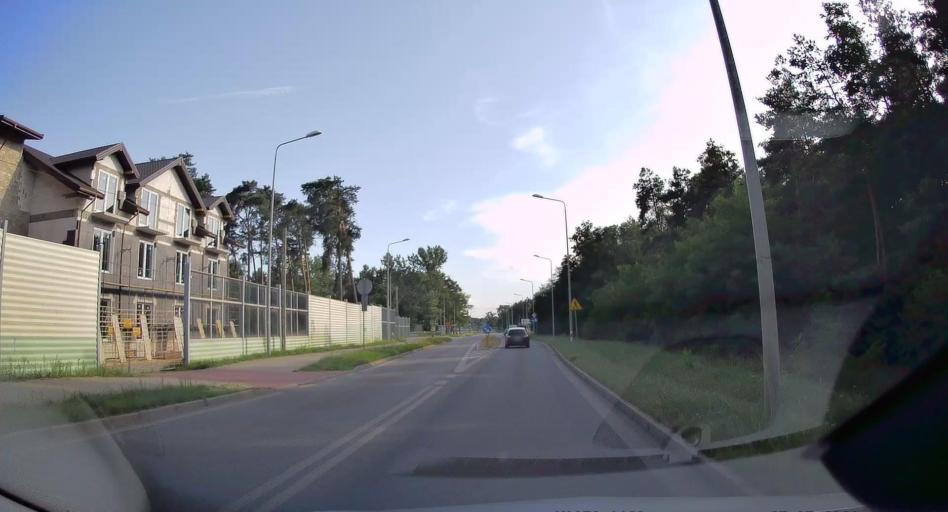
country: PL
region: Swietokrzyskie
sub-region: Powiat konecki
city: Konskie
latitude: 51.1201
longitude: 20.3530
